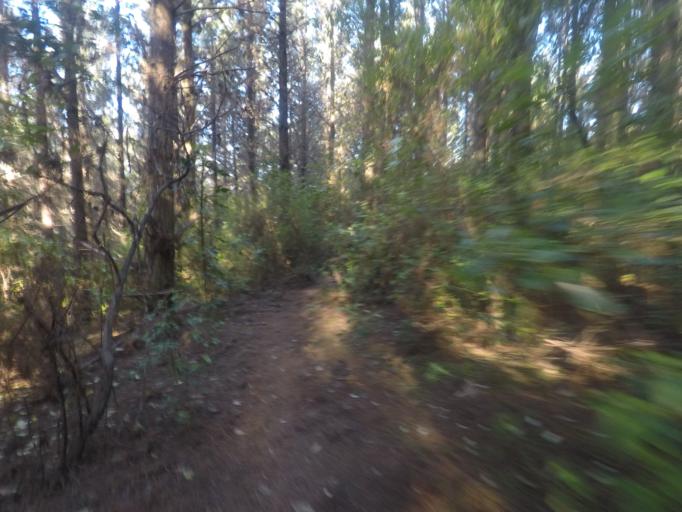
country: NZ
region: Auckland
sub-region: Auckland
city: Muriwai Beach
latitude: -36.7489
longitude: 174.5686
